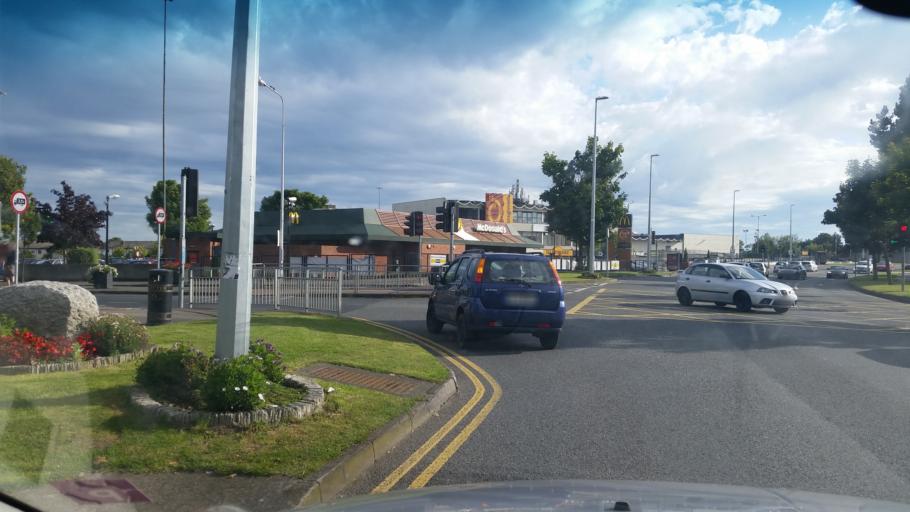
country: IE
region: Leinster
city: Donaghmede
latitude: 53.3964
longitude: -6.1624
